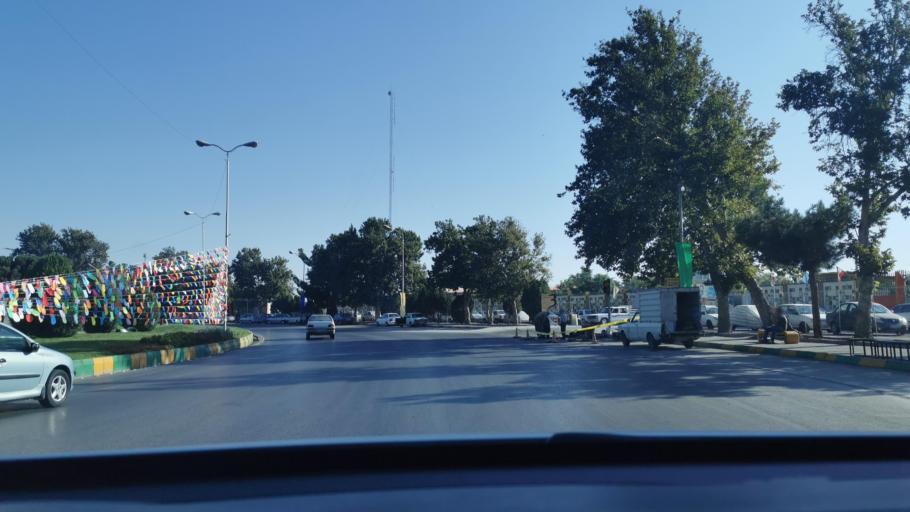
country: IR
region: Razavi Khorasan
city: Mashhad
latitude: 36.3232
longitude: 59.5789
